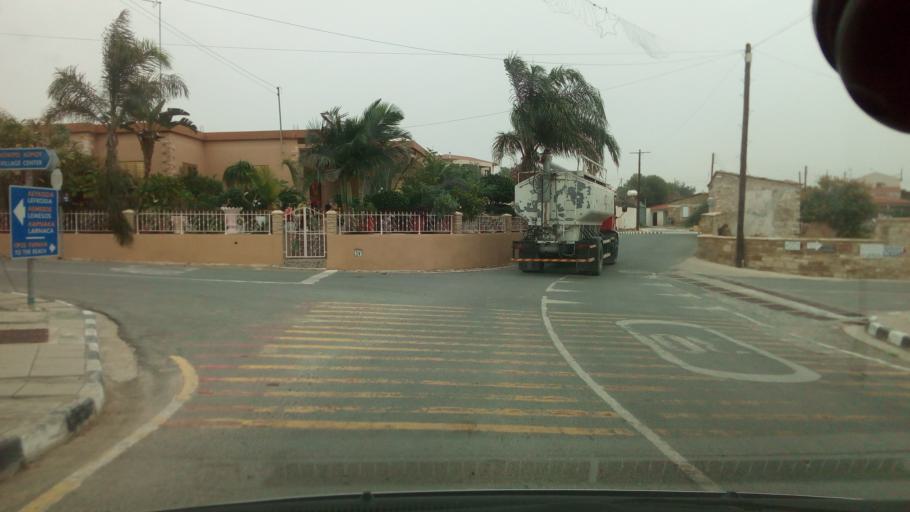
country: CY
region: Larnaka
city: Kofinou
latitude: 34.7584
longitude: 33.3550
